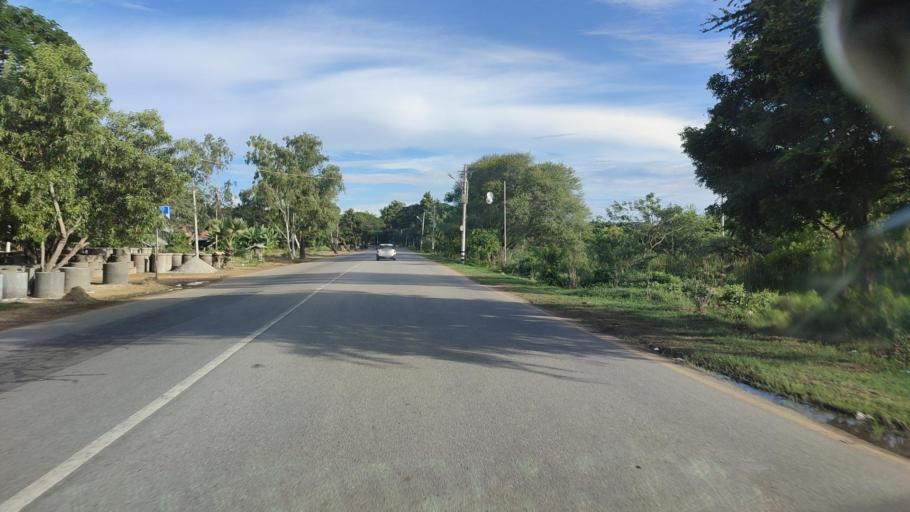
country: MM
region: Mandalay
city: Yamethin
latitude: 20.1465
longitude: 96.1937
